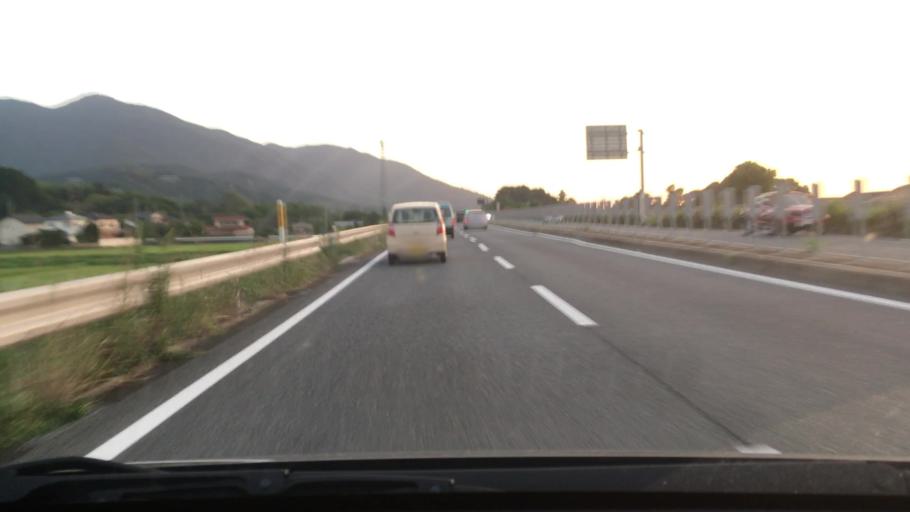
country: JP
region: Fukuoka
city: Maebaru-chuo
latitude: 33.5212
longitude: 130.1648
